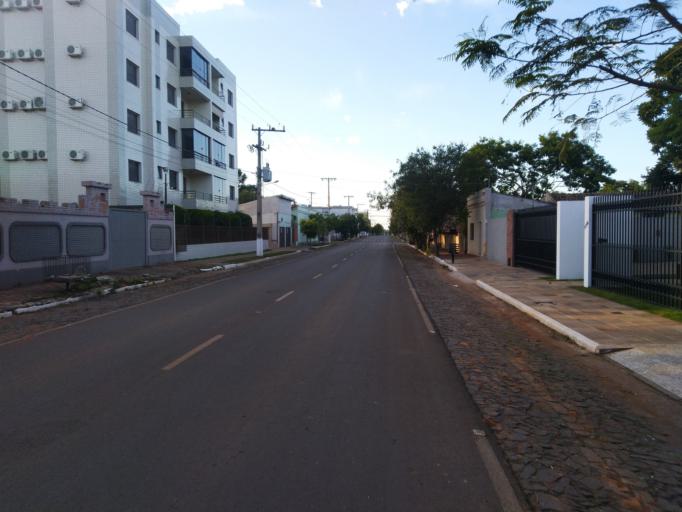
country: BR
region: Rio Grande do Sul
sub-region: Sao Borja
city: Sao Borja
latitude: -28.6606
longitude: -56.0090
